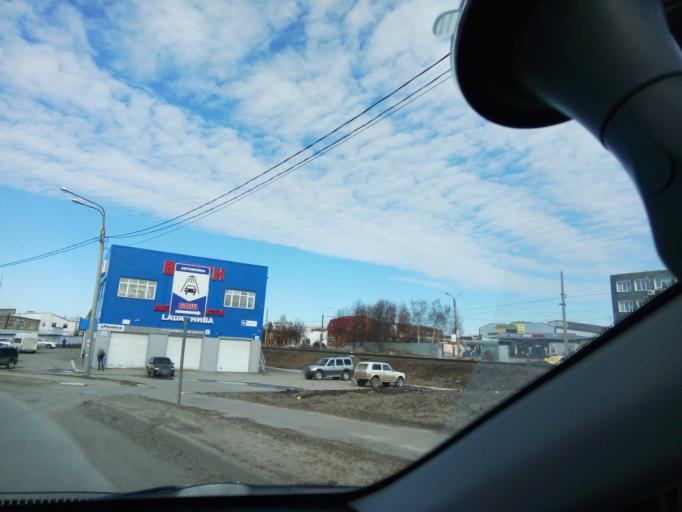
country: RU
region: Chuvashia
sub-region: Cheboksarskiy Rayon
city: Cheboksary
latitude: 56.1020
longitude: 47.2528
